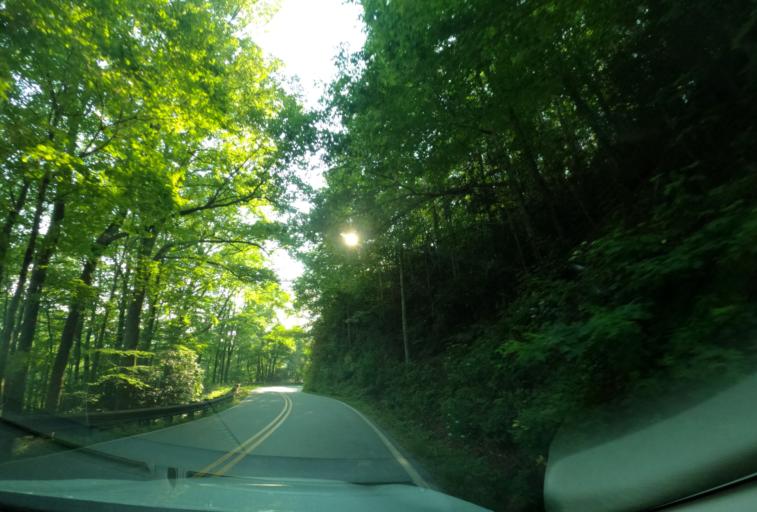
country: US
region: North Carolina
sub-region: Transylvania County
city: Brevard
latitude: 35.1811
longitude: -82.8435
